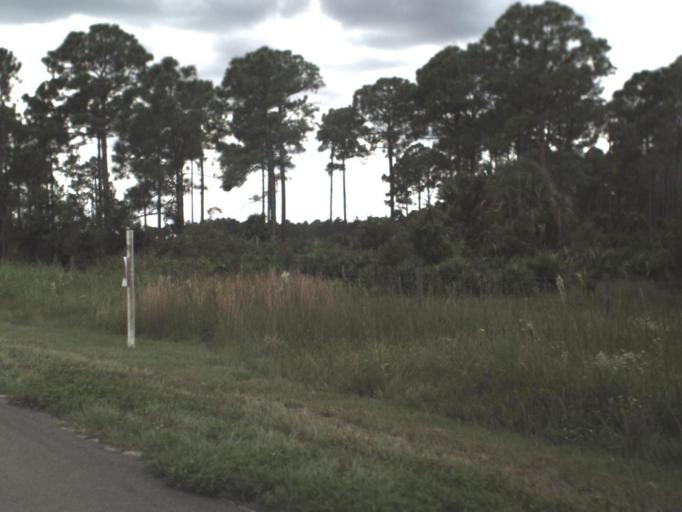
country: US
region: Florida
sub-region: Lee County
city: Olga
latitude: 26.8467
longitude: -81.7598
